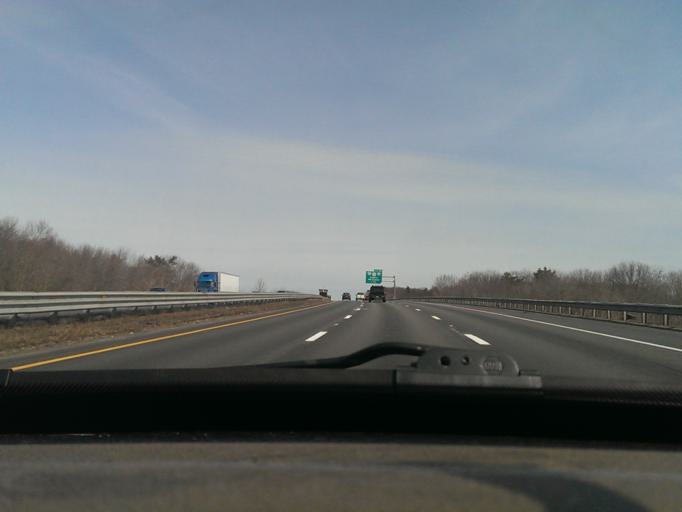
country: US
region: Massachusetts
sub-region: Worcester County
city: Auburn
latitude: 42.1871
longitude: -71.8752
